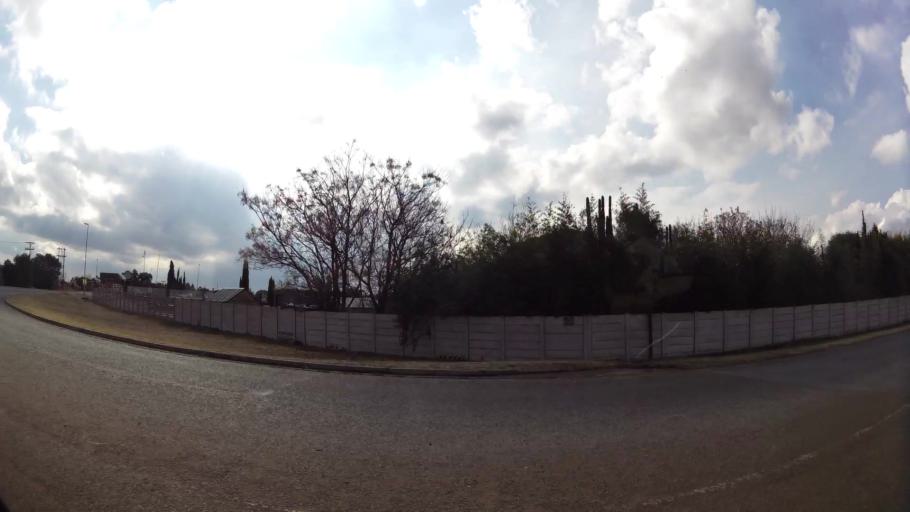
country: ZA
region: Gauteng
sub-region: Sedibeng District Municipality
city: Vanderbijlpark
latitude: -26.7402
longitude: 27.8202
